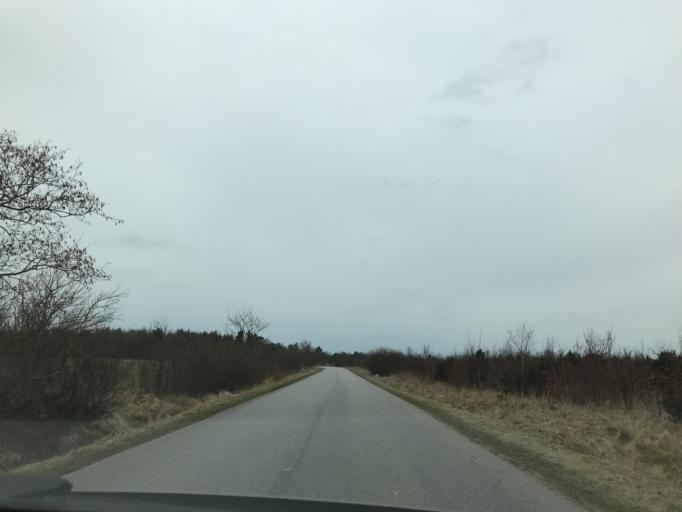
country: DK
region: South Denmark
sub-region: Varde Kommune
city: Oksbol
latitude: 55.8044
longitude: 8.3325
